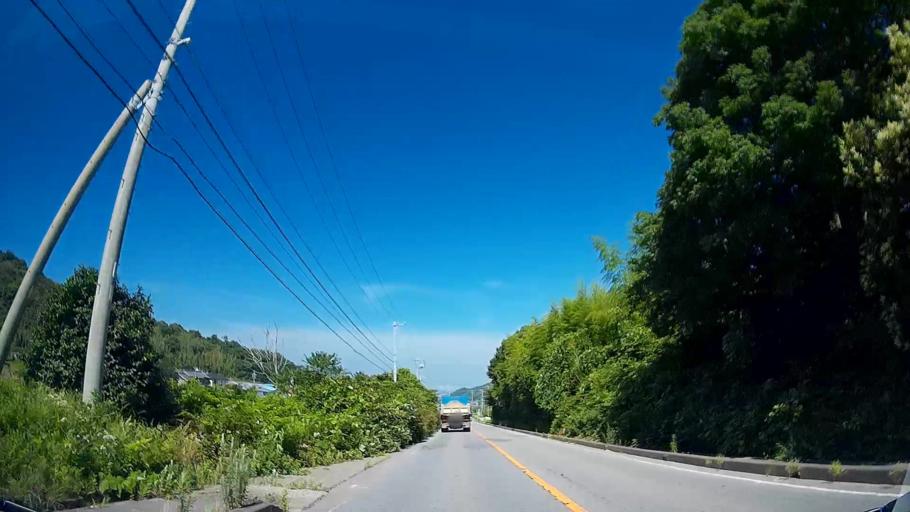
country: JP
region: Aichi
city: Nishio
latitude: 34.8293
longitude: 137.1369
